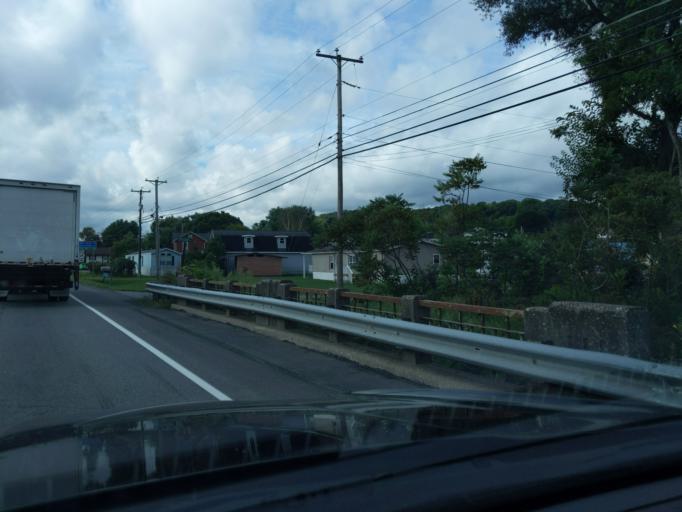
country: US
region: Pennsylvania
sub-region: Blair County
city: Roaring Spring
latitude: 40.3579
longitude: -78.4302
